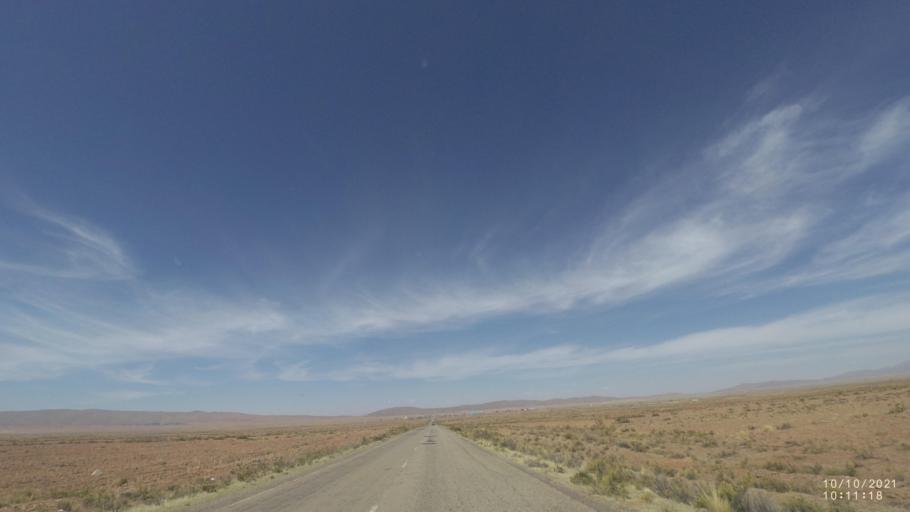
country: BO
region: La Paz
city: Eucaliptus
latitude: -17.4211
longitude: -67.5019
